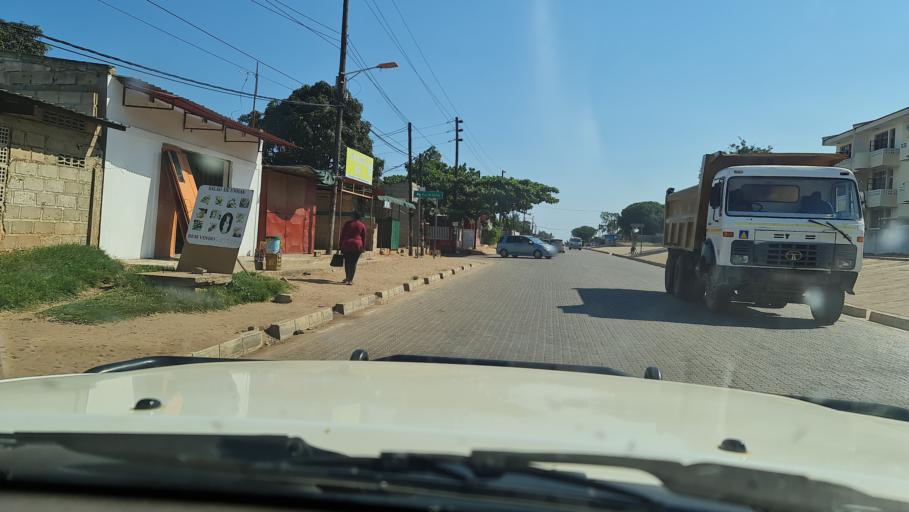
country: MZ
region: Maputo City
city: Maputo
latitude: -25.8396
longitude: 32.6363
